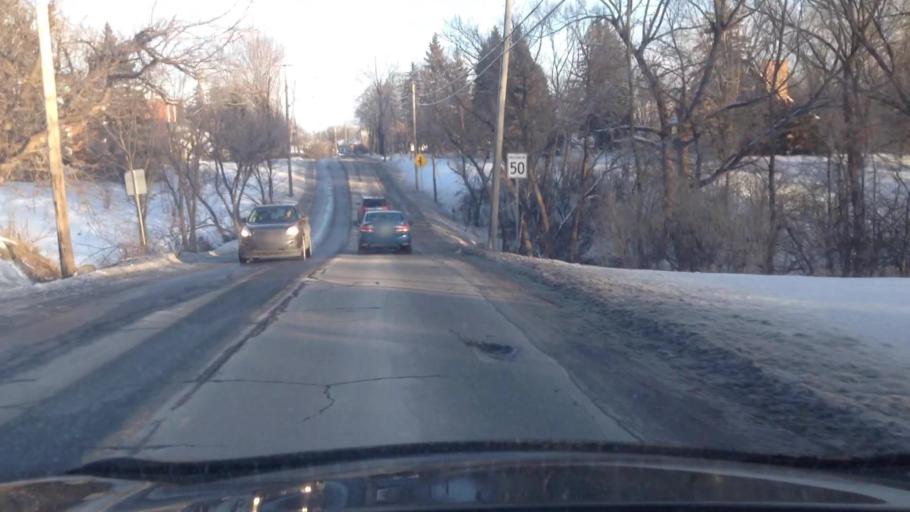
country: CA
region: Quebec
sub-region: Lanaudiere
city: Saint-Lin-Laurentides
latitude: 45.8519
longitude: -73.7637
